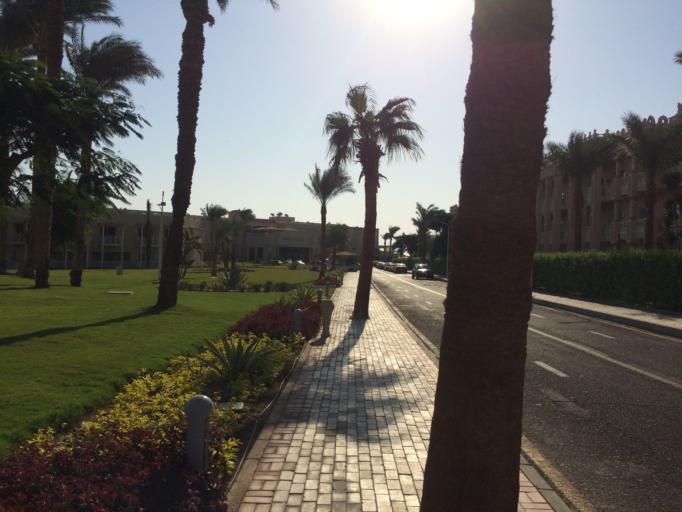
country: EG
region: Red Sea
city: Hurghada
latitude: 27.1214
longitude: 33.8264
